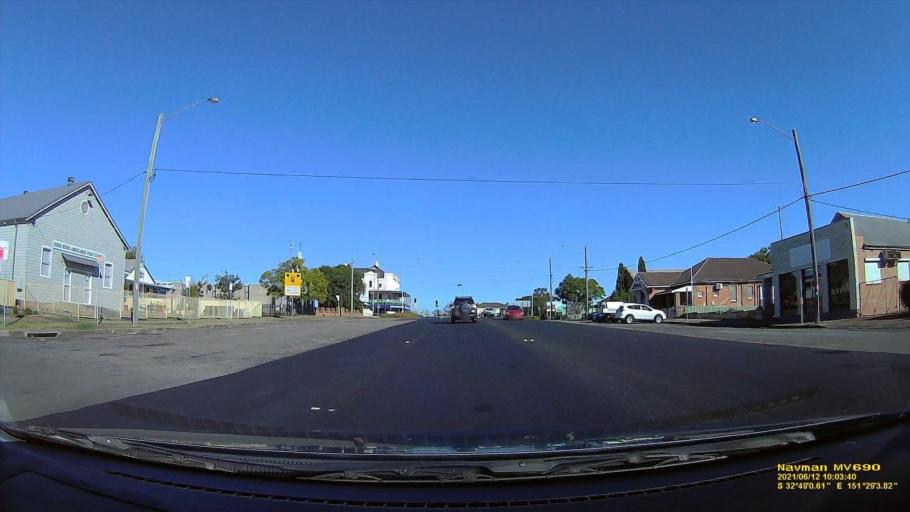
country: AU
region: New South Wales
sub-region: Cessnock
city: Kurri Kurri
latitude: -32.8169
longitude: 151.4842
